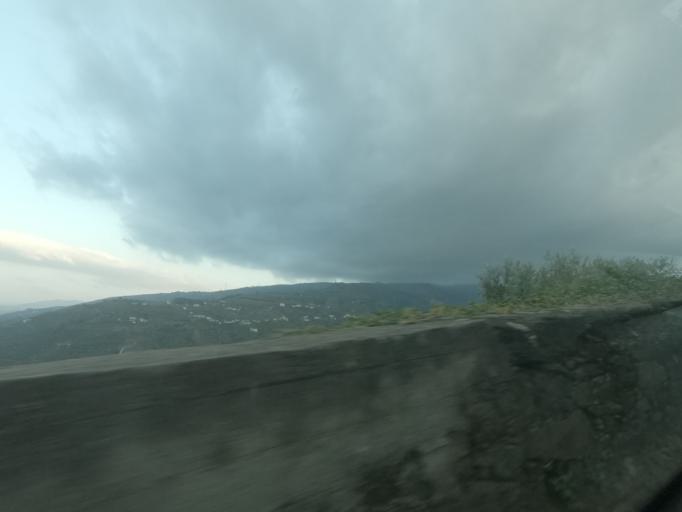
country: PT
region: Vila Real
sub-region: Mesao Frio
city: Mesao Frio
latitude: 41.1581
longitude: -7.8828
